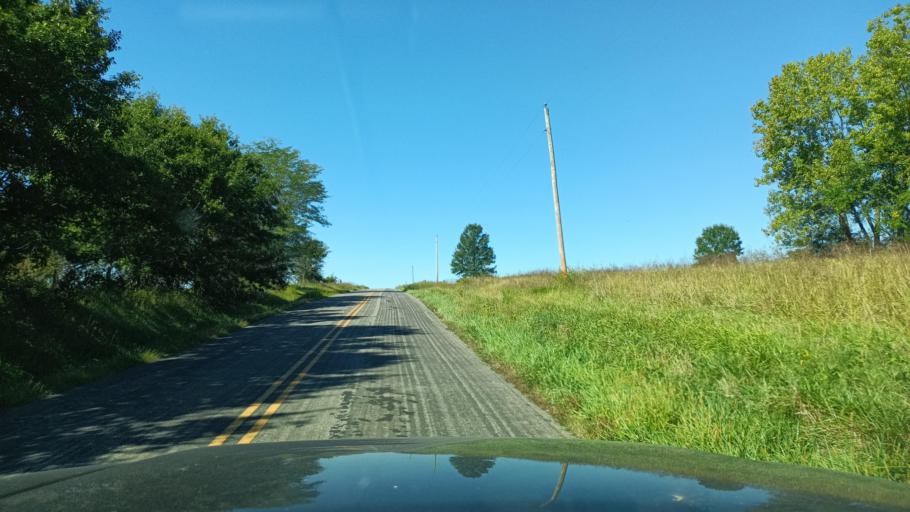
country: US
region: Missouri
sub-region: Scotland County
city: Memphis
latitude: 40.3543
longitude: -92.2816
